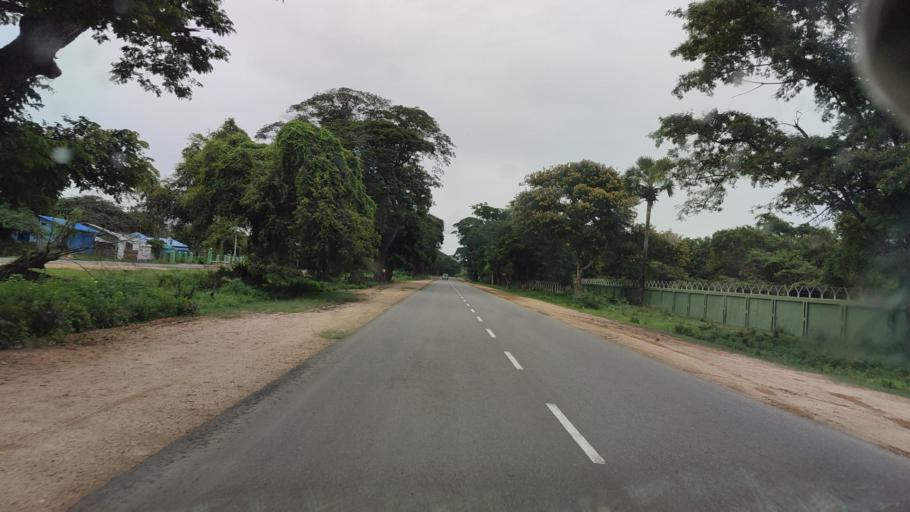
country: MM
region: Mandalay
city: Meiktila
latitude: 20.7881
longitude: 95.9080
